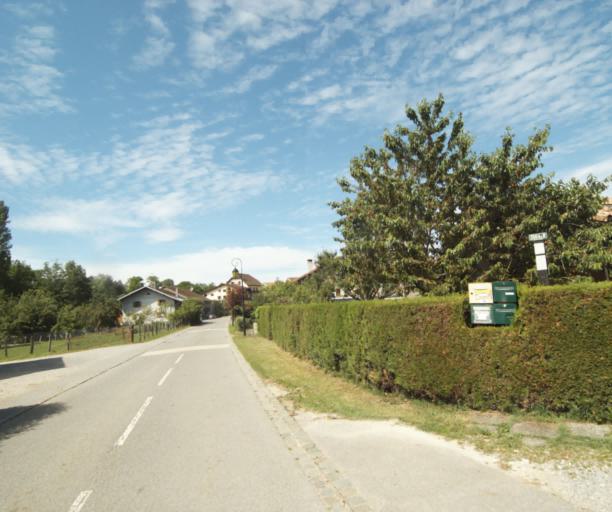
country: FR
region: Rhone-Alpes
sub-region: Departement de la Haute-Savoie
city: Perrignier
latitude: 46.2843
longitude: 6.4174
